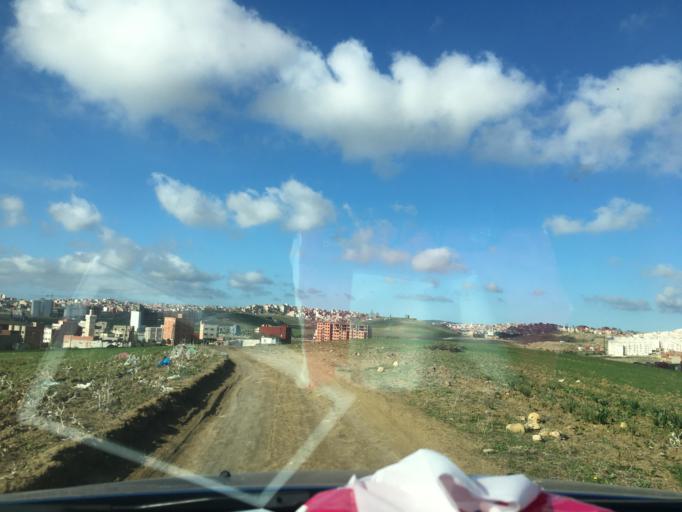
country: MA
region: Tanger-Tetouan
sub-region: Tanger-Assilah
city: Tangier
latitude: 35.7175
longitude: -5.8170
